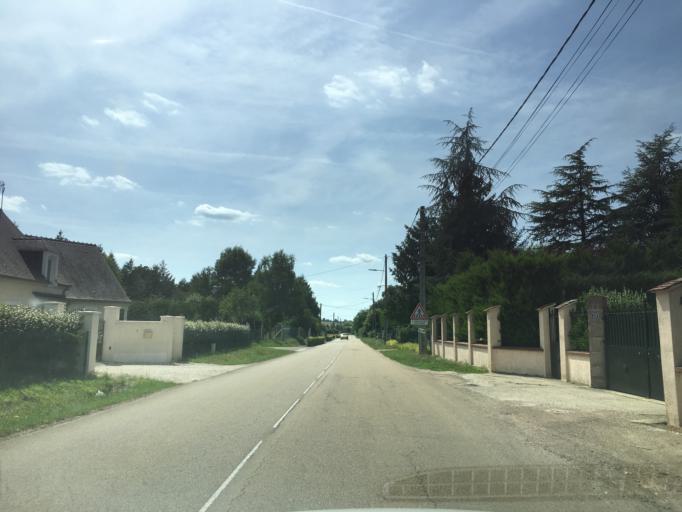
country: FR
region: Bourgogne
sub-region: Departement de l'Yonne
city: Charbuy
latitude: 47.8001
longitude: 3.4445
